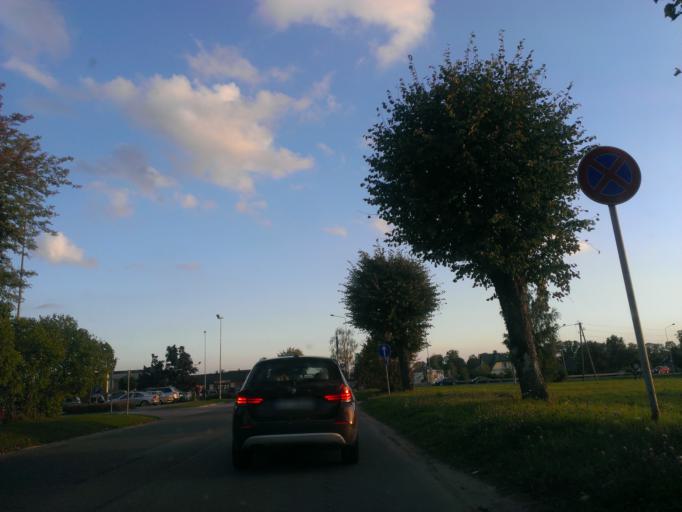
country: LV
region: Sigulda
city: Sigulda
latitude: 57.1435
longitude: 24.8437
